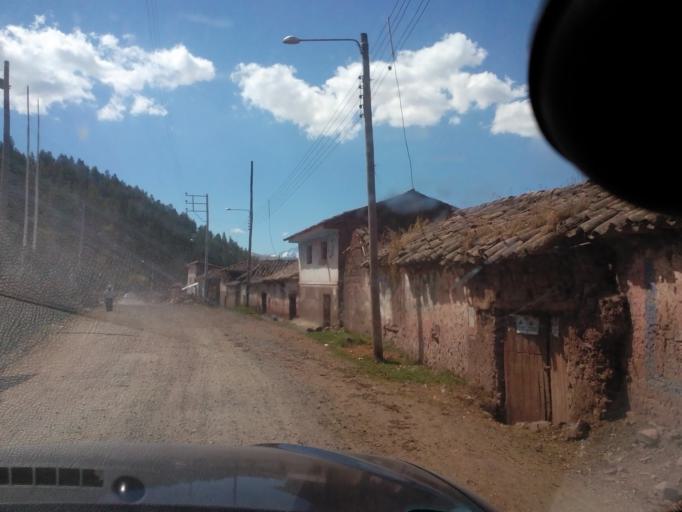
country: PE
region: Cusco
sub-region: Provincia de Anta
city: Huarocondo
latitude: -13.4353
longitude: -72.2252
